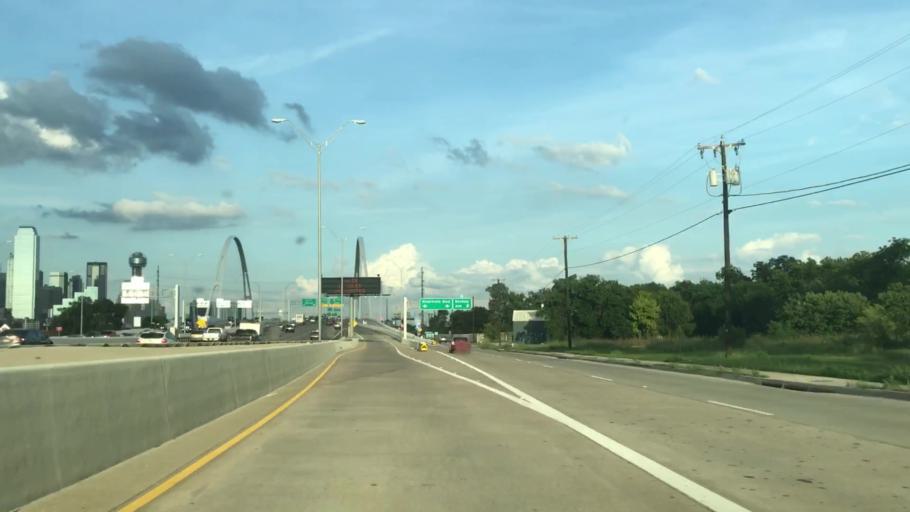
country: US
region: Texas
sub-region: Dallas County
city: Dallas
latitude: 32.7681
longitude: -96.8271
